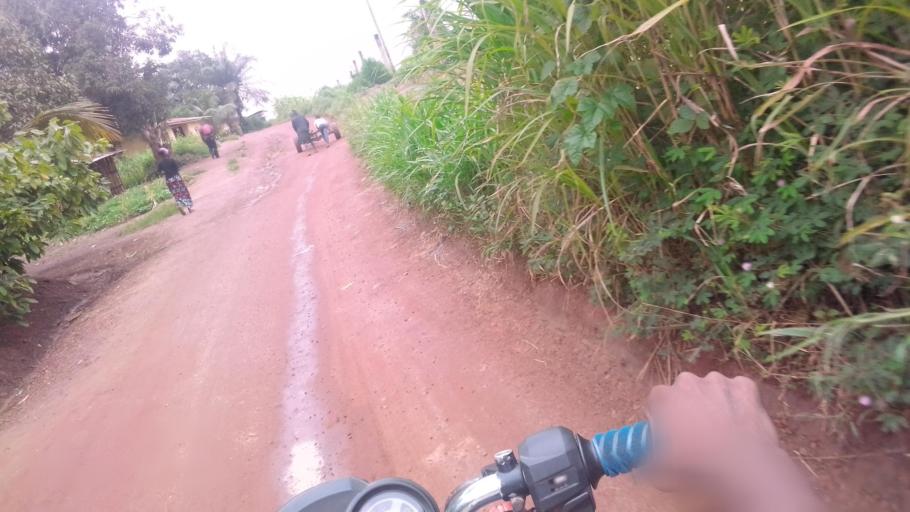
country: SL
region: Eastern Province
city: Kenema
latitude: 7.8657
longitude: -11.1729
